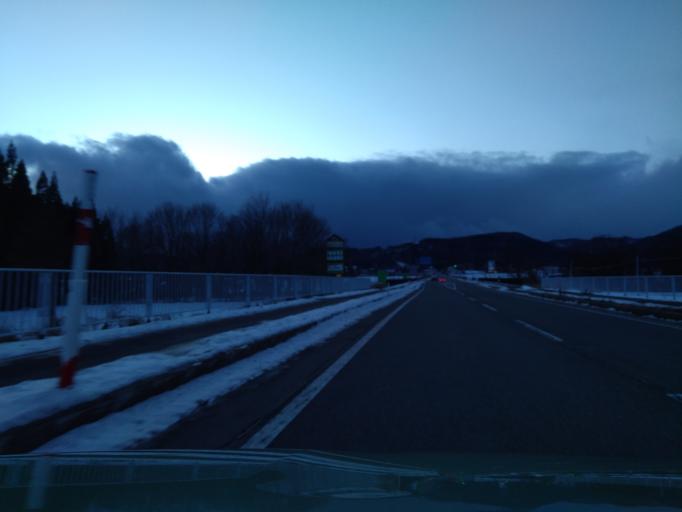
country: JP
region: Iwate
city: Shizukuishi
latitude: 39.6978
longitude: 140.9498
